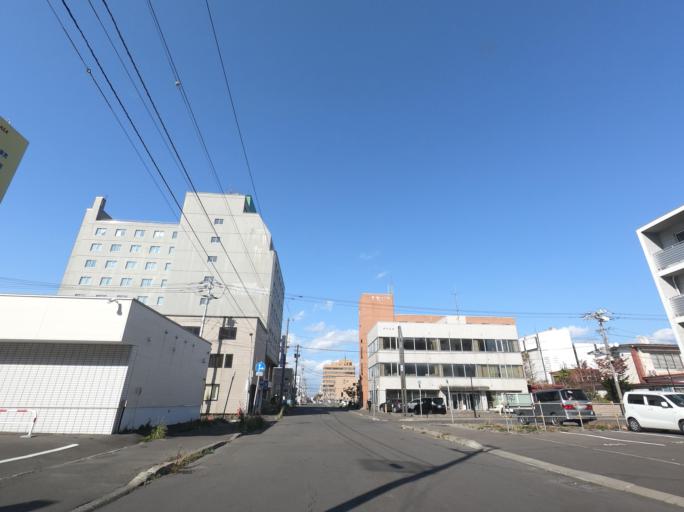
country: JP
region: Hokkaido
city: Kushiro
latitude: 42.9822
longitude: 144.3834
